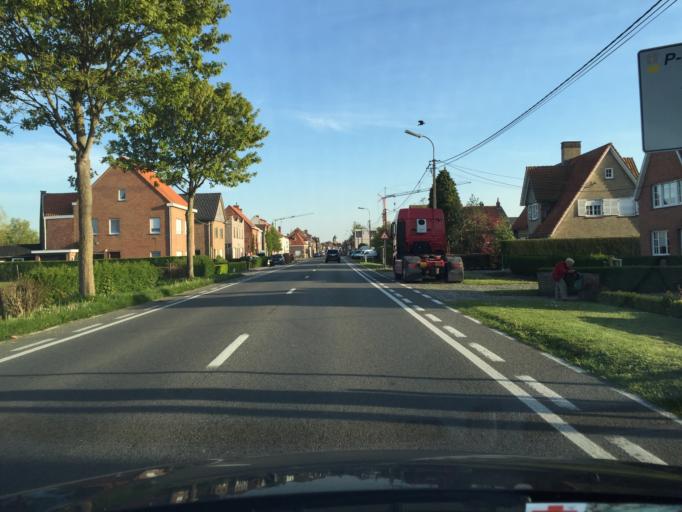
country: BE
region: Flanders
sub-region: Provincie Oost-Vlaanderen
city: Maldegem
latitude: 51.2199
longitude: 3.4471
